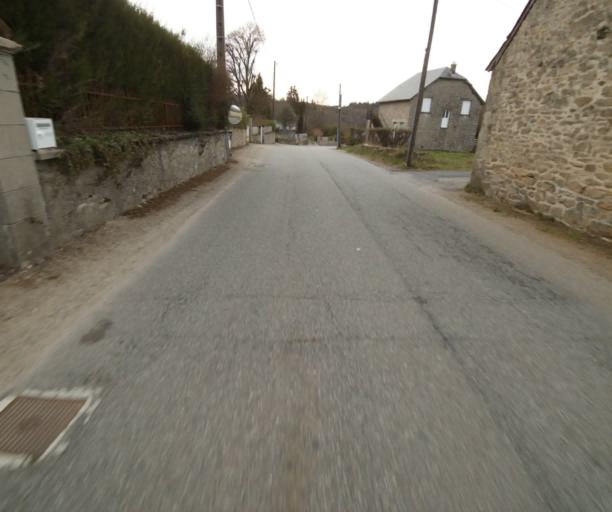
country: FR
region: Limousin
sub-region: Departement de la Correze
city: Correze
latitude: 45.4234
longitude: 1.8393
